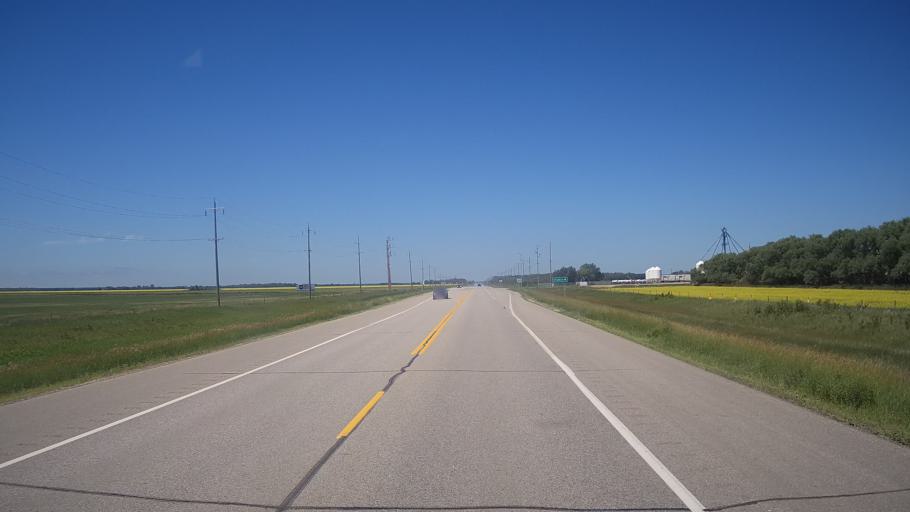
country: CA
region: Manitoba
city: Neepawa
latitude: 50.2257
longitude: -99.0727
